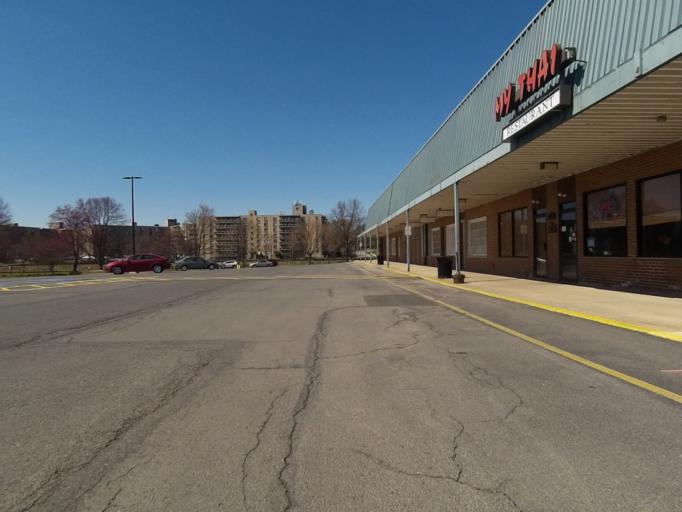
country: US
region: Pennsylvania
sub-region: Centre County
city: State College
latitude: 40.7833
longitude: -77.8519
